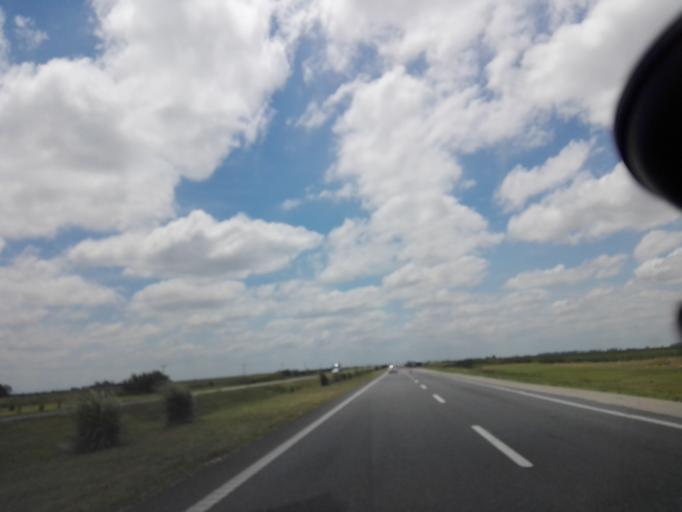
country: AR
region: Cordoba
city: Oncativo
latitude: -31.8226
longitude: -63.7105
